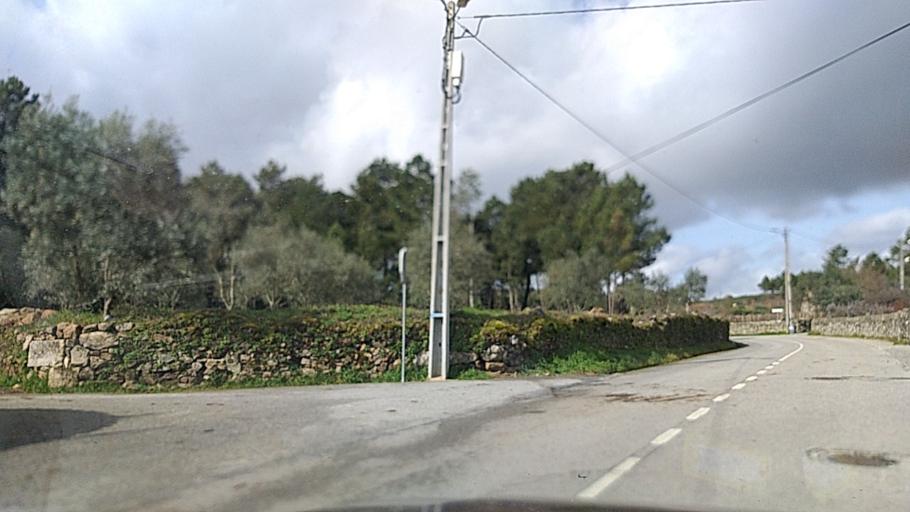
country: PT
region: Guarda
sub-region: Fornos de Algodres
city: Fornos de Algodres
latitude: 40.6627
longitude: -7.5705
